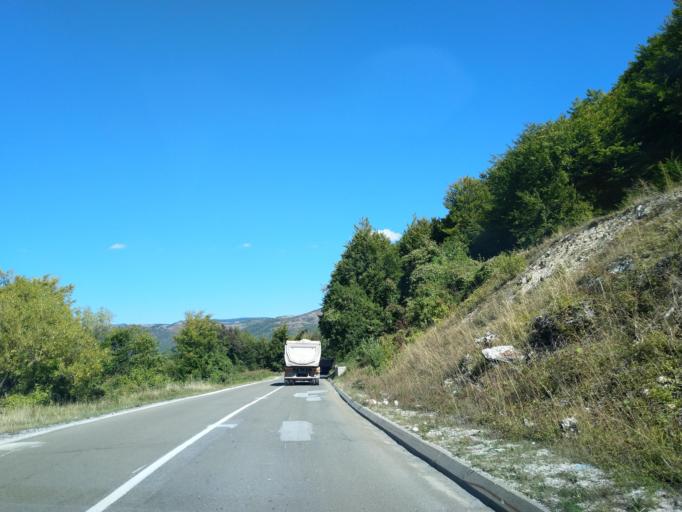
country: RS
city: Sokolovica
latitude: 43.2500
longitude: 20.2412
